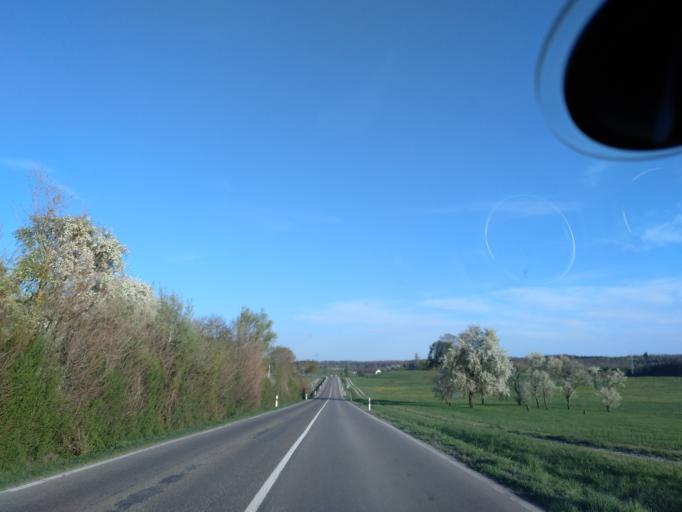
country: DE
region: Baden-Wuerttemberg
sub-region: Regierungsbezirk Stuttgart
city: Kirchberg an der Jagst
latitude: 49.1484
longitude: 9.9784
